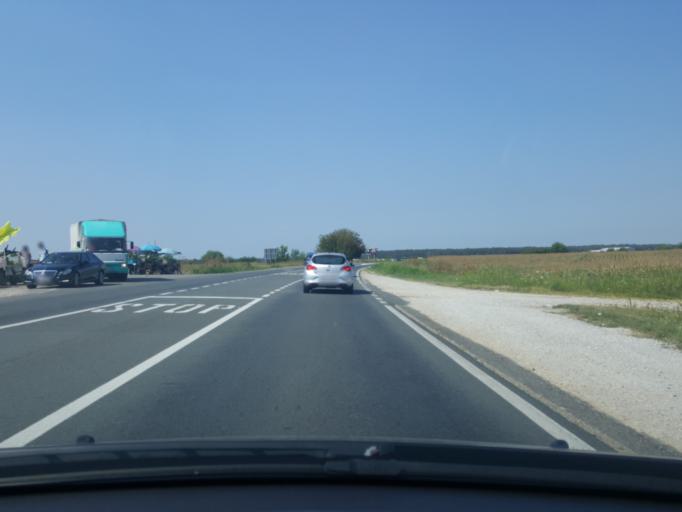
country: RS
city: Klenak
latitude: 44.7849
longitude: 19.7232
